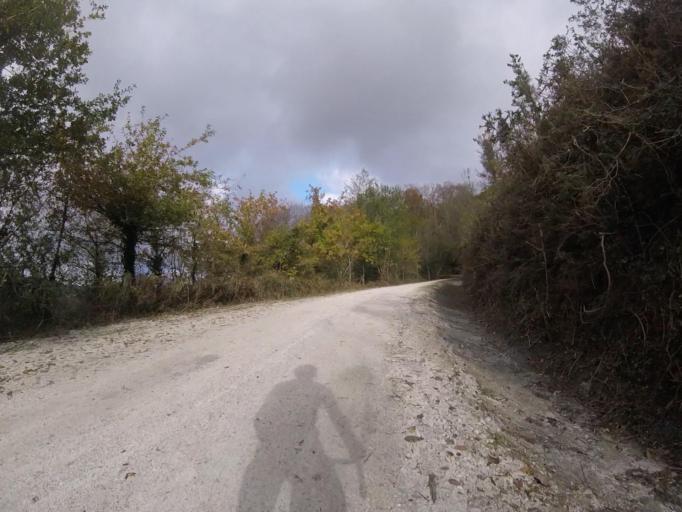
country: ES
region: Navarre
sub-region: Provincia de Navarra
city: Goizueta
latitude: 43.2059
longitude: -1.8543
